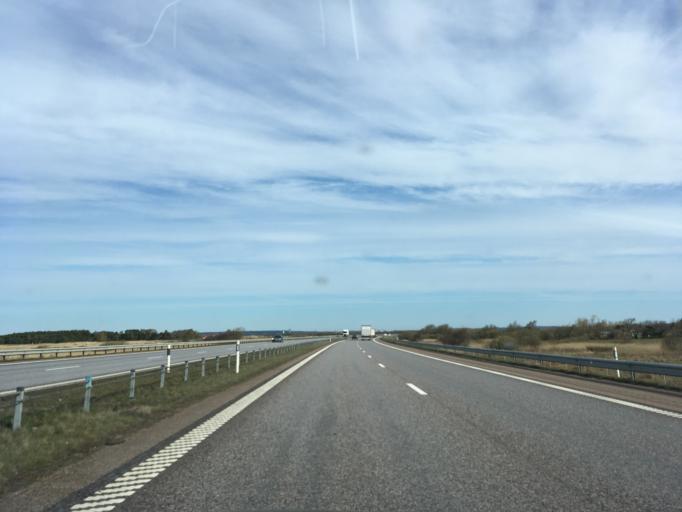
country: SE
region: Halland
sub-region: Halmstads Kommun
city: Troenninge
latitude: 56.6096
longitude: 12.9188
